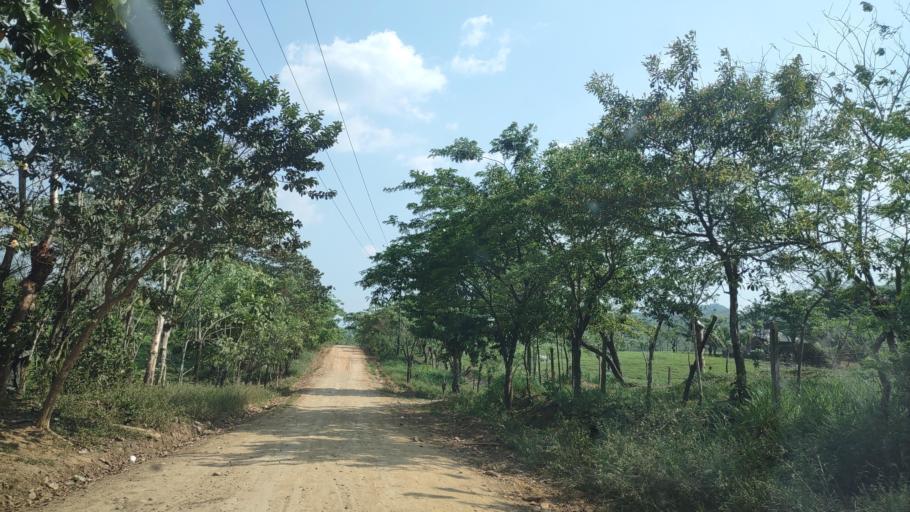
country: MX
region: Chiapas
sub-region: Tecpatan
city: Raudales Malpaso
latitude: 17.3447
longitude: -93.7553
